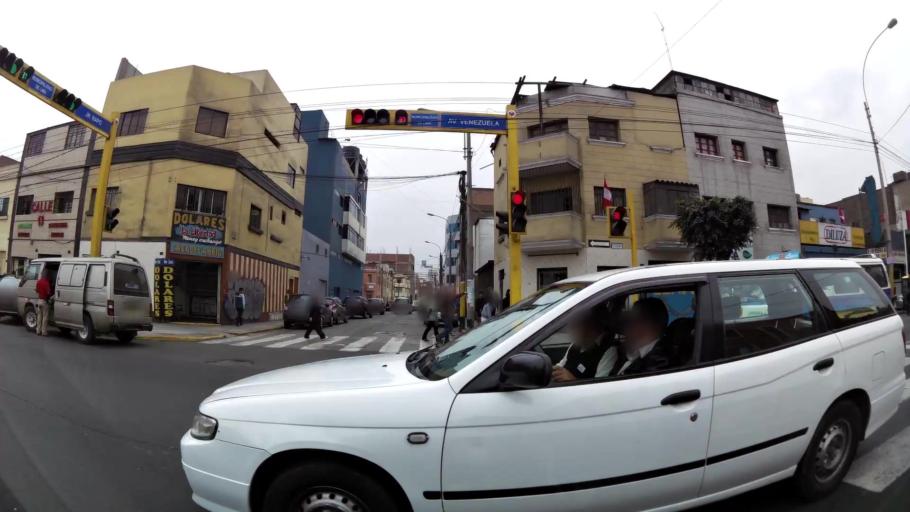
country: PE
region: Lima
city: Lima
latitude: -12.0554
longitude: -77.0524
